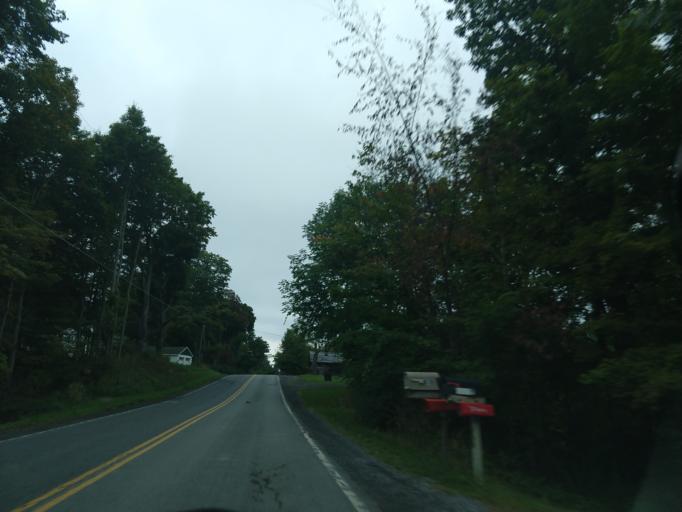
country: US
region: New York
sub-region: Tompkins County
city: East Ithaca
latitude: 42.4074
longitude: -76.4686
